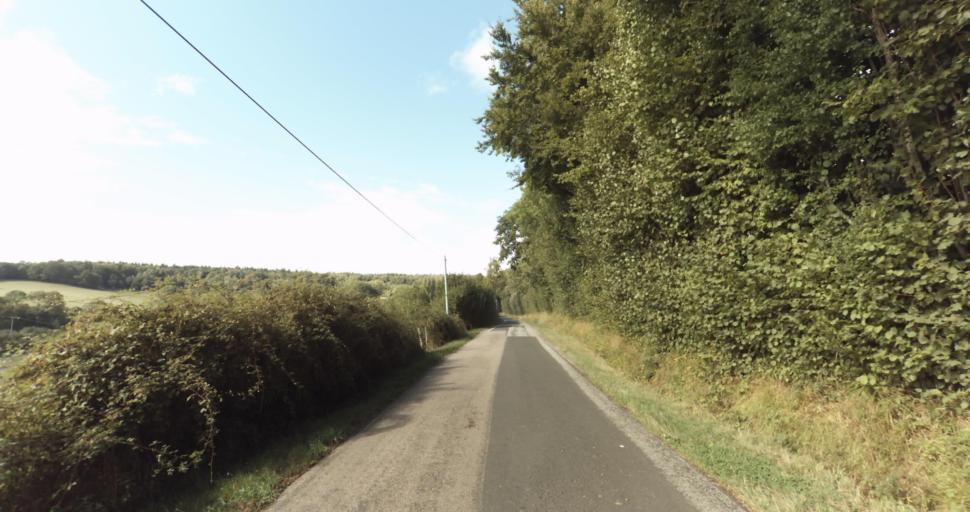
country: FR
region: Lower Normandy
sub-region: Departement de l'Orne
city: Gace
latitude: 48.7761
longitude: 0.3343
